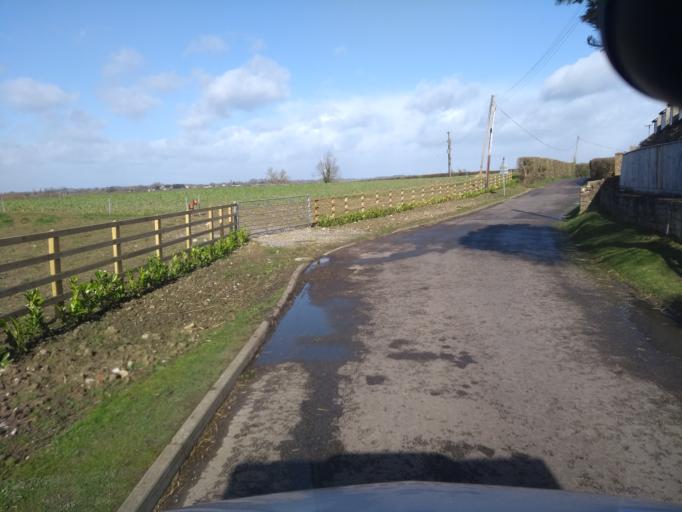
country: GB
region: England
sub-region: Somerset
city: South Petherton
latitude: 50.9766
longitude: -2.8451
